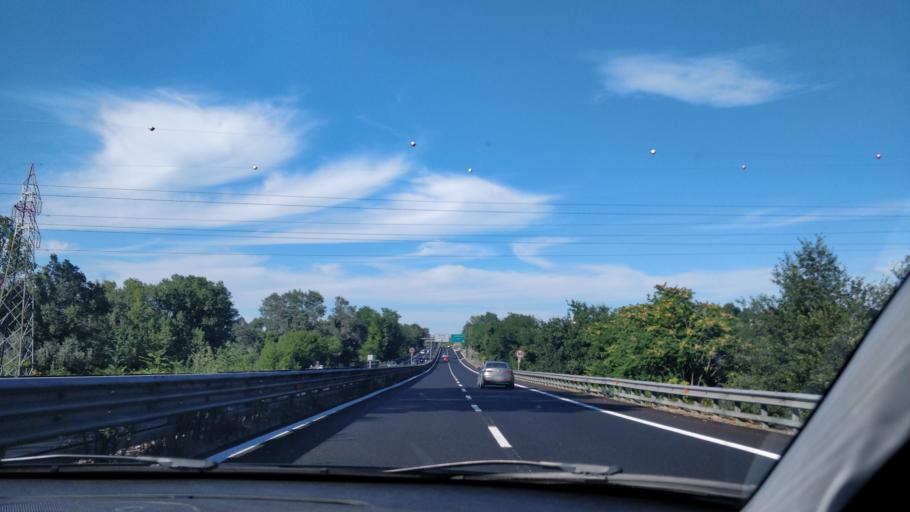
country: IT
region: Abruzzo
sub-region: Provincia di Chieti
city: Chieti
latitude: 42.3911
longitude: 14.1558
